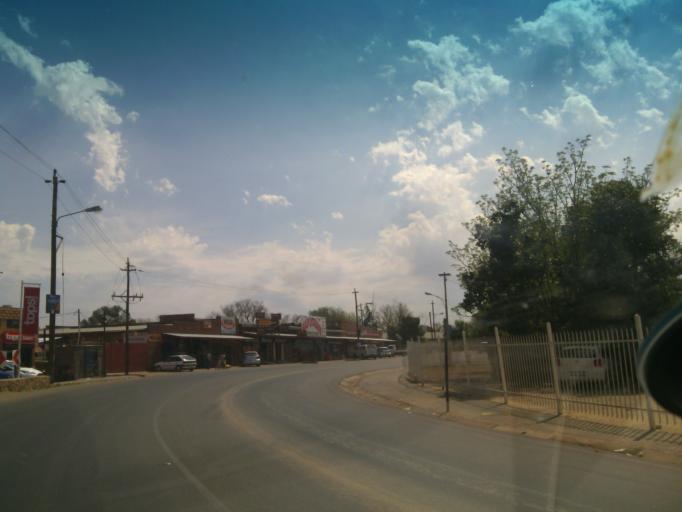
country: ZA
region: Northern Cape
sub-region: Frances Baard District Municipality
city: Barkly West
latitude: -28.5384
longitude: 24.5183
